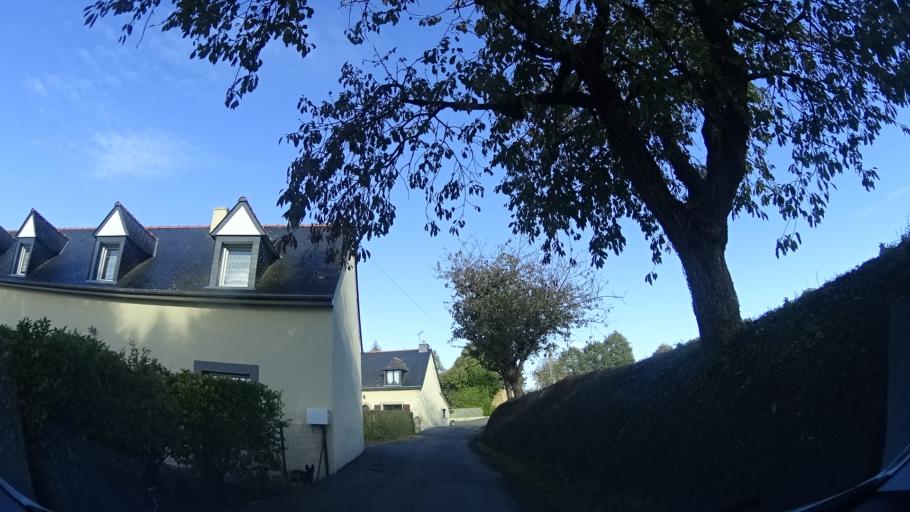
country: FR
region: Brittany
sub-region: Departement d'Ille-et-Vilaine
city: Geveze
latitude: 48.2012
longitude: -1.7823
